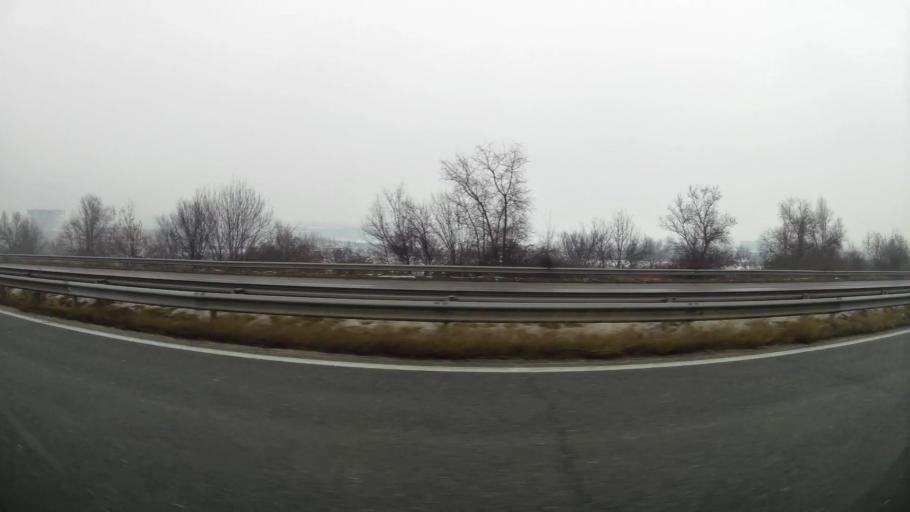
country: MK
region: Petrovec
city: Petrovec
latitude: 41.9544
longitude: 21.6307
